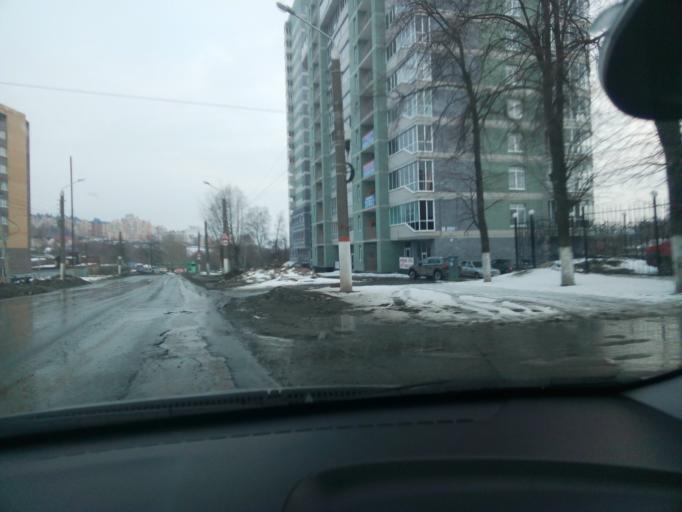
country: RU
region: Chuvashia
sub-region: Cheboksarskiy Rayon
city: Cheboksary
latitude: 56.1337
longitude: 47.2231
